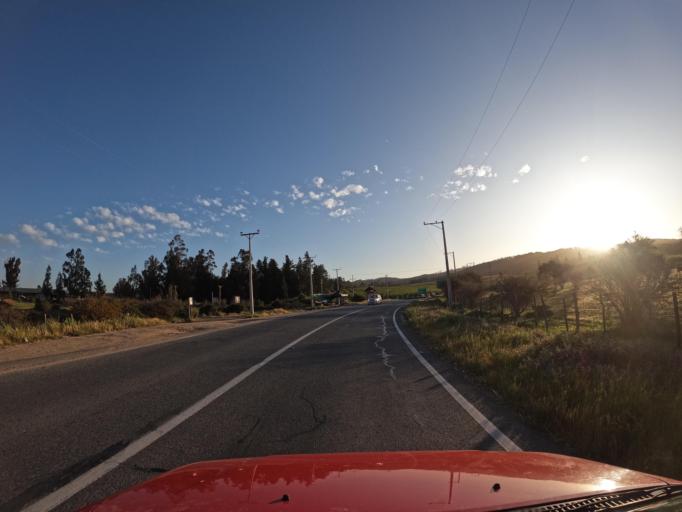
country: CL
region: O'Higgins
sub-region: Provincia de Colchagua
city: Santa Cruz
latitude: -34.3309
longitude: -71.7464
